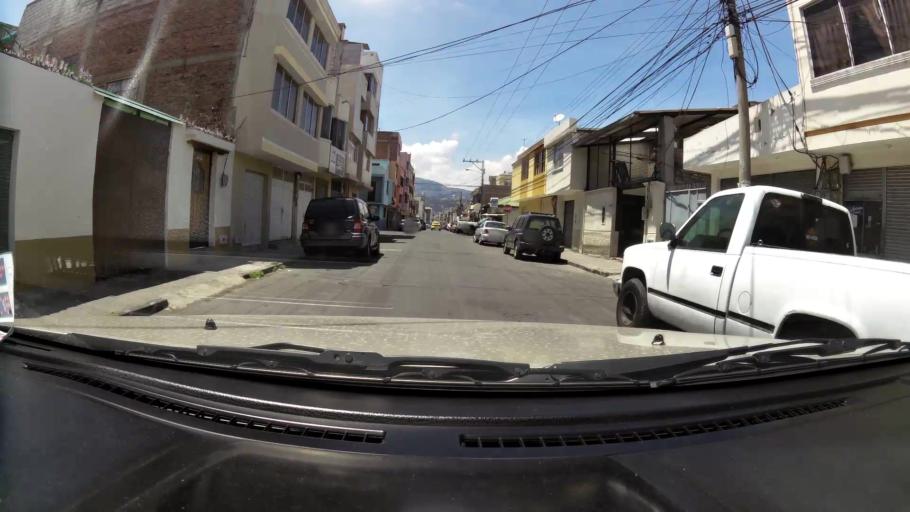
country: EC
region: Chimborazo
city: Riobamba
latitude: -1.6644
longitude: -78.6533
